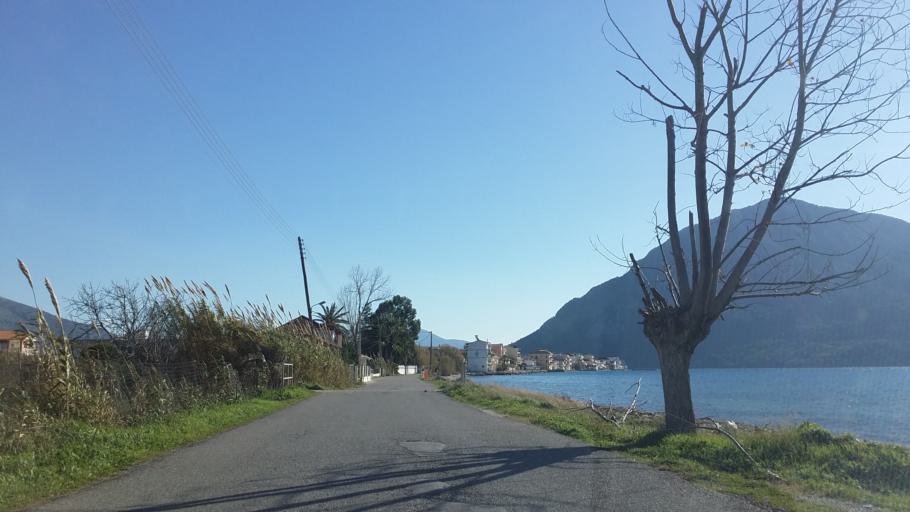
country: GR
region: West Greece
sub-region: Nomos Aitolias kai Akarnanias
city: Kandila
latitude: 38.6747
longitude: 20.9400
